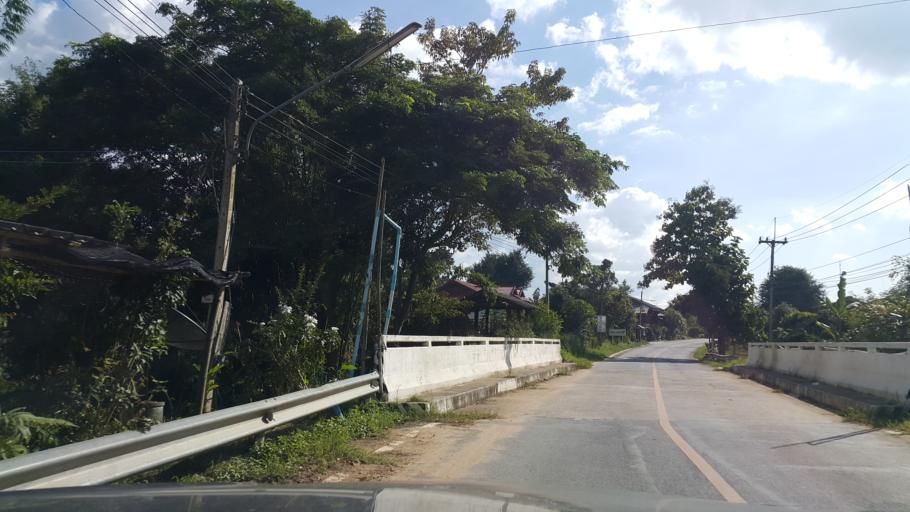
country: TH
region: Lamphun
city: Ban Thi
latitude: 18.5897
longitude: 99.2659
